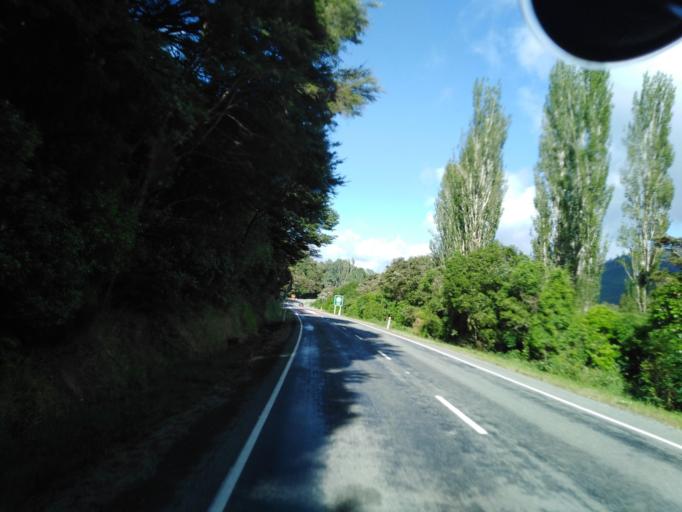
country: NZ
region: Nelson
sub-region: Nelson City
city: Nelson
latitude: -41.3004
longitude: 173.5813
